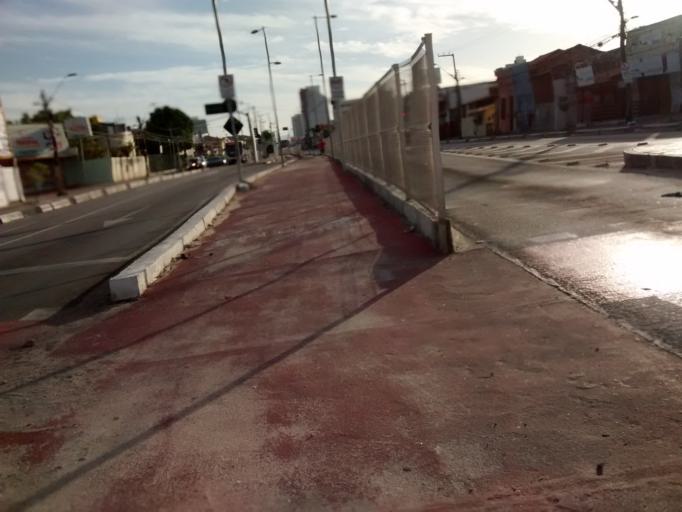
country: BR
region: Ceara
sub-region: Fortaleza
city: Fortaleza
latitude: -3.7322
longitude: -38.5476
